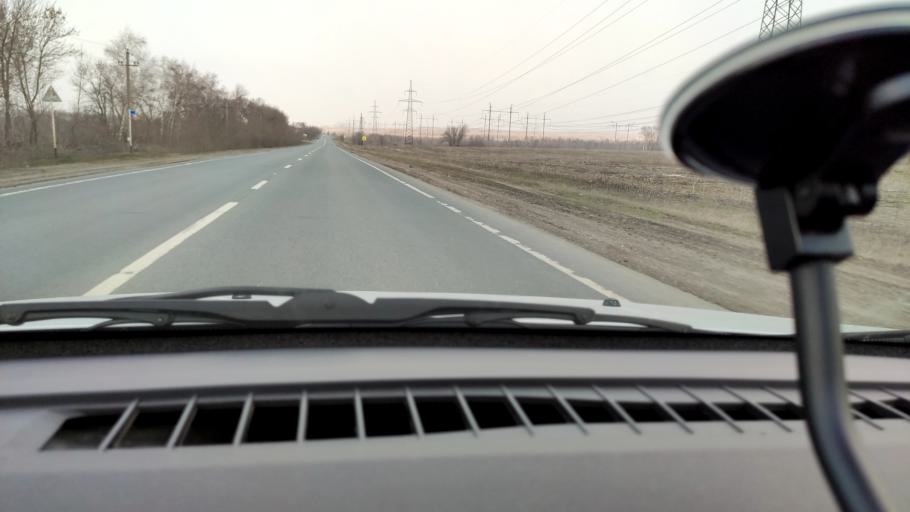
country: RU
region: Samara
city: Dubovyy Umet
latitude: 53.0794
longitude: 50.3888
